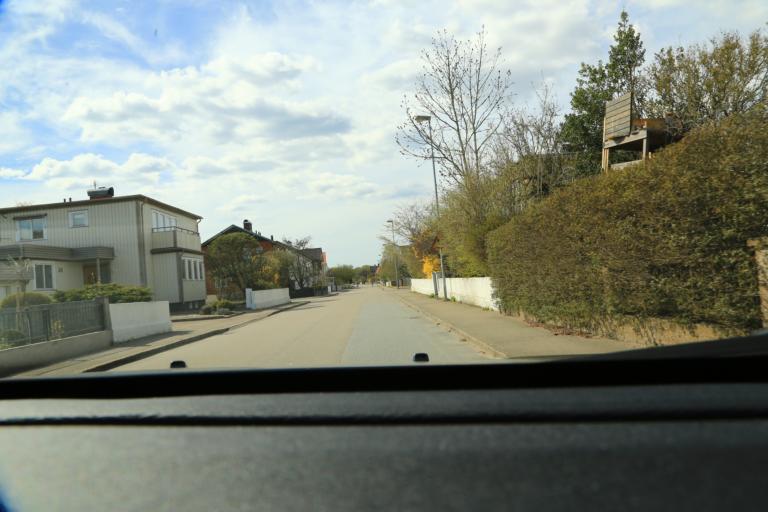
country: SE
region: Halland
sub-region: Varbergs Kommun
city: Varberg
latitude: 57.1009
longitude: 12.2685
